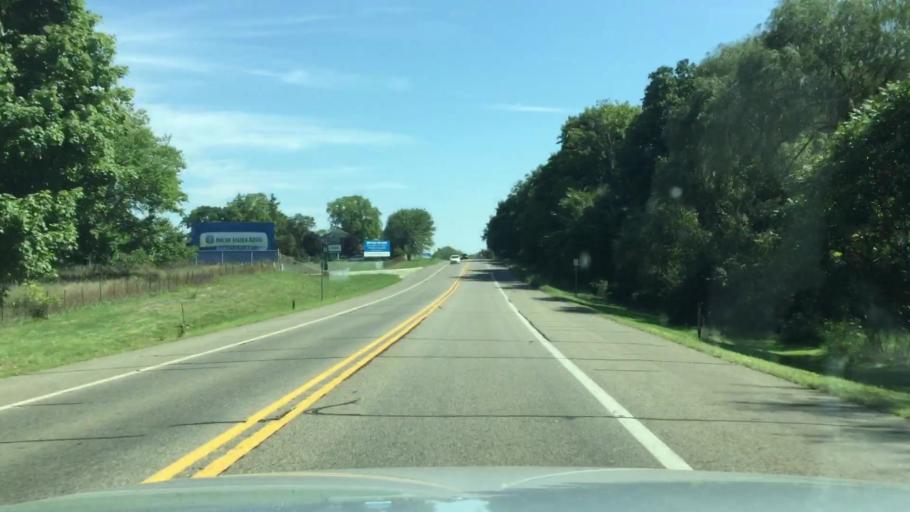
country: US
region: Michigan
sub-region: Jackson County
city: Brooklyn
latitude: 42.0569
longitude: -84.2531
